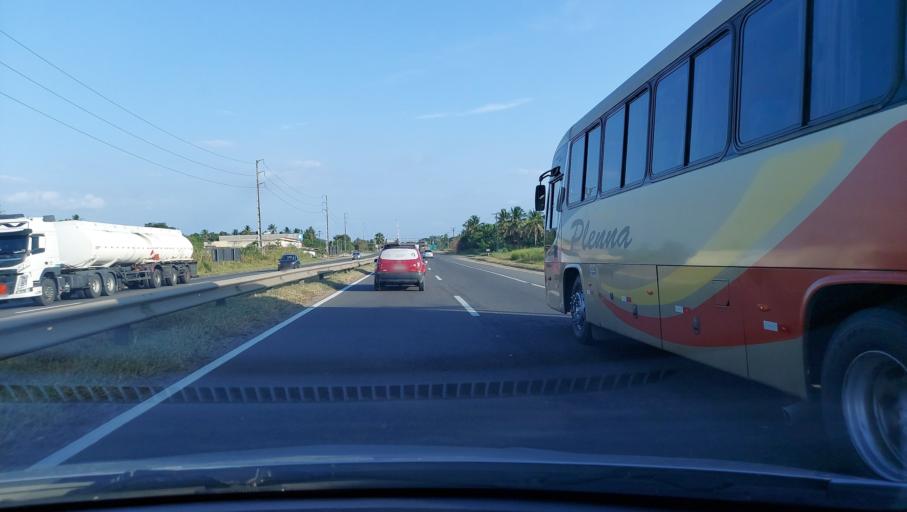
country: BR
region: Bahia
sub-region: Conceicao Do Jacuipe
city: Conceicao do Jacuipe
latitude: -12.3803
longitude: -38.7991
